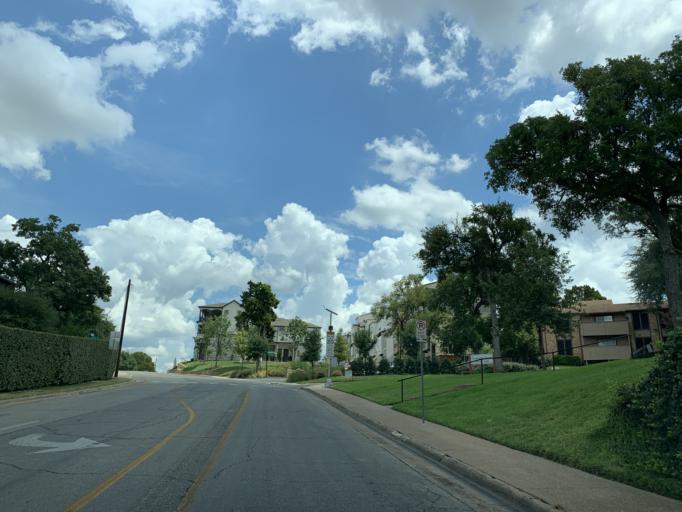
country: US
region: Texas
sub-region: Dallas County
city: Cockrell Hill
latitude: 32.7516
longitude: -96.8521
